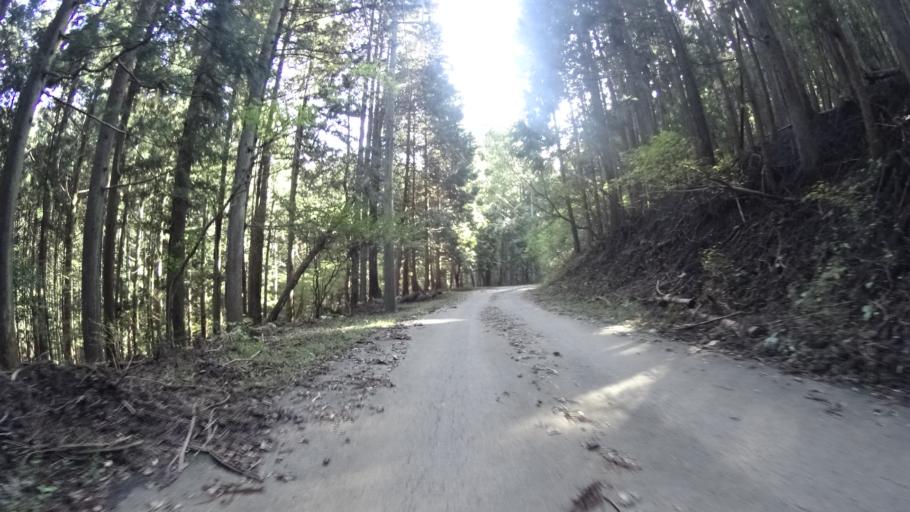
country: JP
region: Yamanashi
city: Otsuki
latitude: 35.5789
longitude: 138.9775
